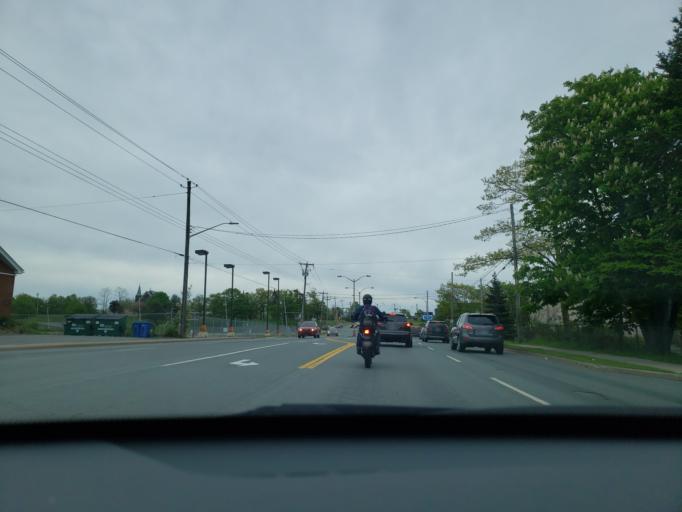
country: CA
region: Nova Scotia
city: Dartmouth
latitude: 44.6840
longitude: -63.5316
